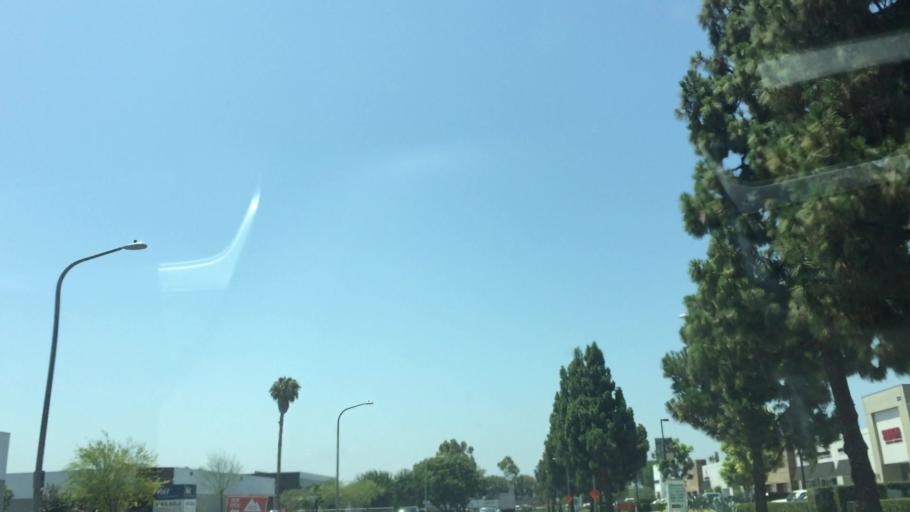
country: US
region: California
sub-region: Orange County
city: Fountain Valley
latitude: 33.6954
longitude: -117.9250
